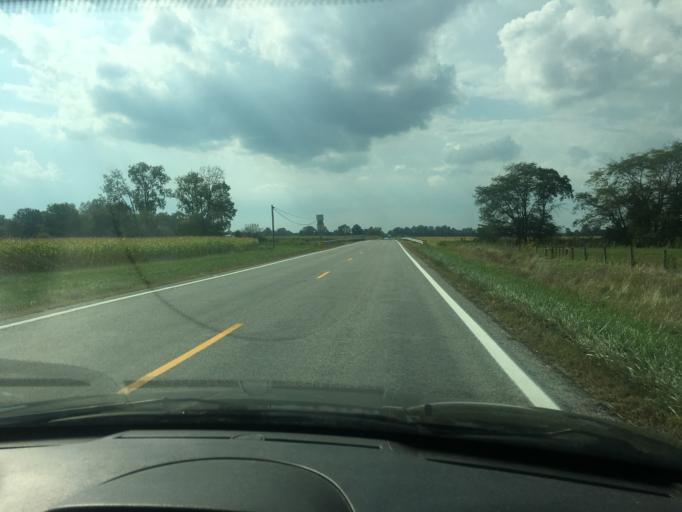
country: US
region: Ohio
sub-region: Champaign County
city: Urbana
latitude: 40.1555
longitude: -83.7479
